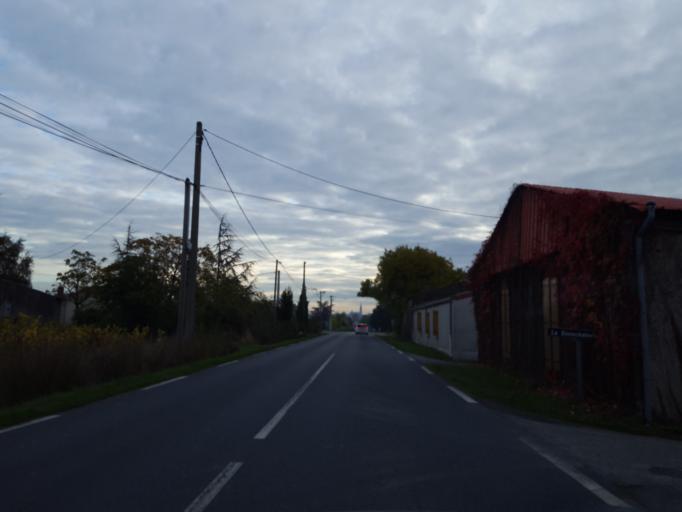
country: FR
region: Pays de la Loire
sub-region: Departement de la Loire-Atlantique
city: Saint-Julien-de-Concelles
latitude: 47.2348
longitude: -1.3867
